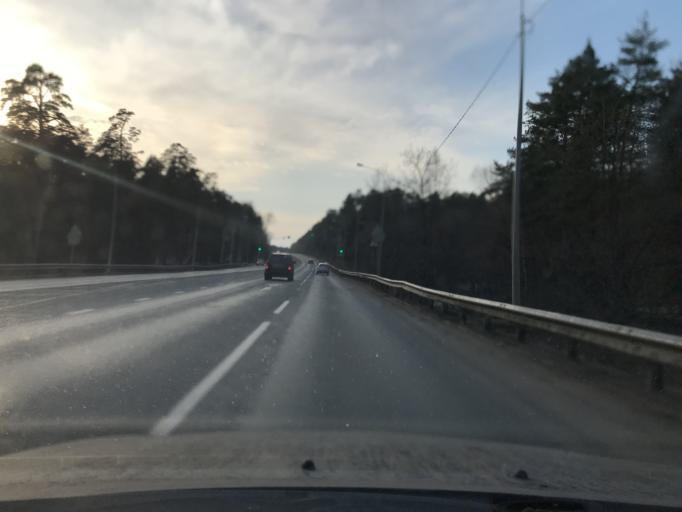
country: RU
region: Kaluga
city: Mstikhino
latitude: 54.5217
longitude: 36.1943
